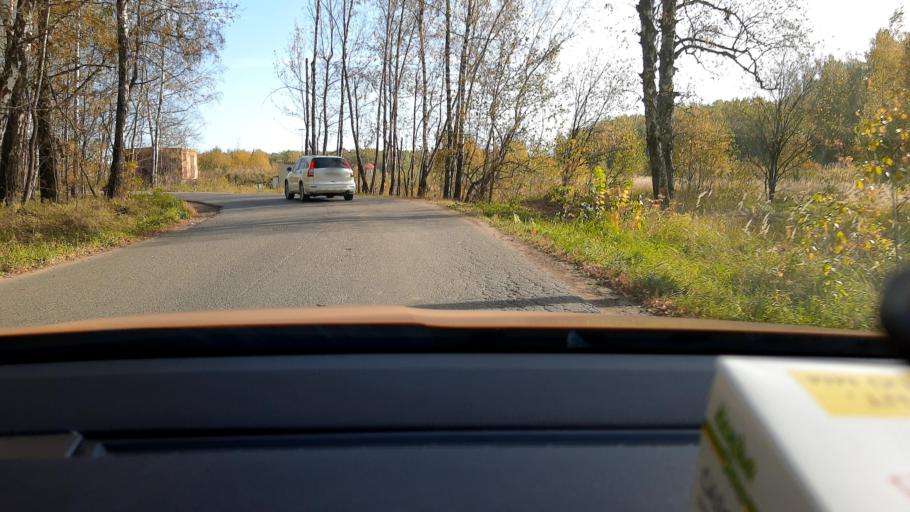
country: RU
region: Moskovskaya
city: Gorki-Leninskiye
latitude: 55.5271
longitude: 37.7883
